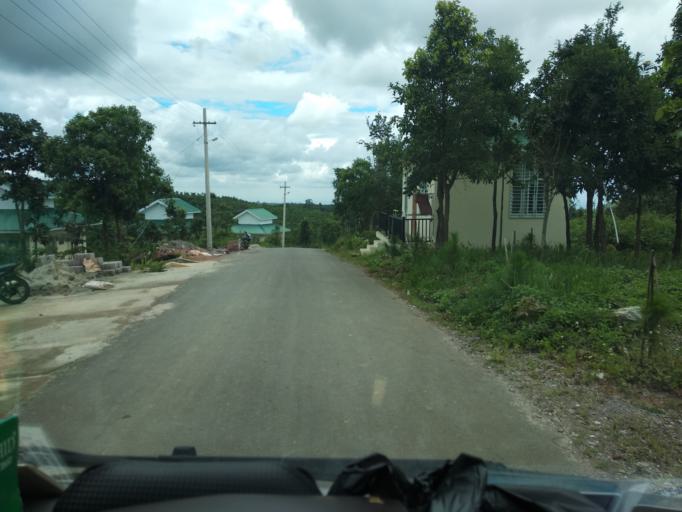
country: MM
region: Mandalay
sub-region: Pyin Oo Lwin District
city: Pyin Oo Lwin
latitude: 21.9104
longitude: 96.3855
